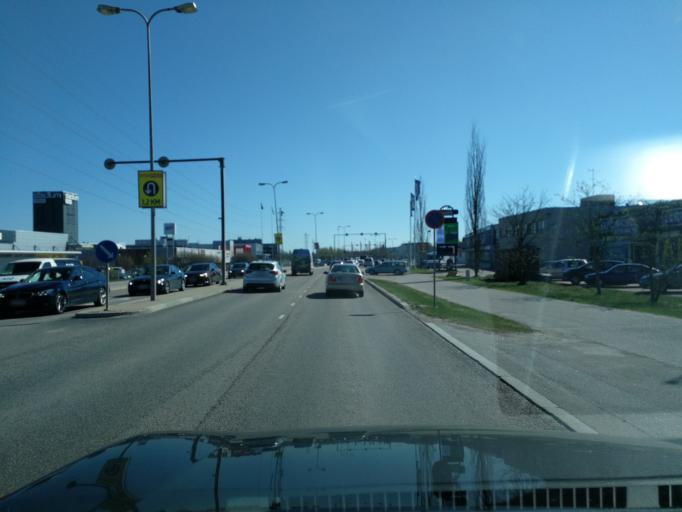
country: FI
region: Uusimaa
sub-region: Helsinki
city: Vantaa
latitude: 60.2757
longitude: 24.9705
